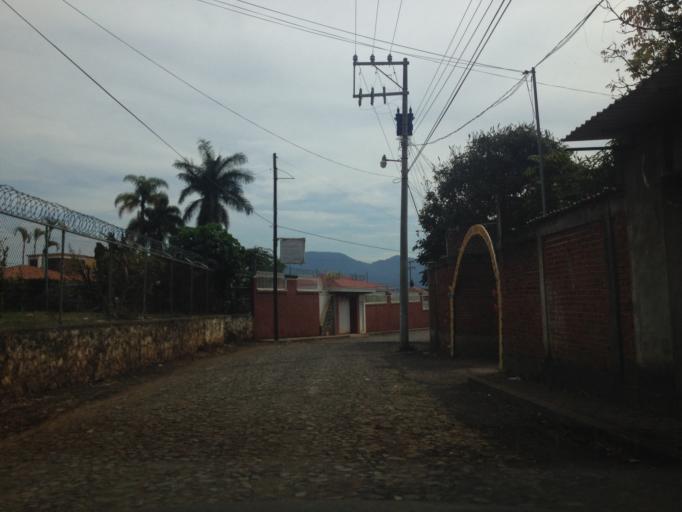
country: MX
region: Michoacan
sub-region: Ziracuaretiro
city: Patuan
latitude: 19.4323
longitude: -101.9248
